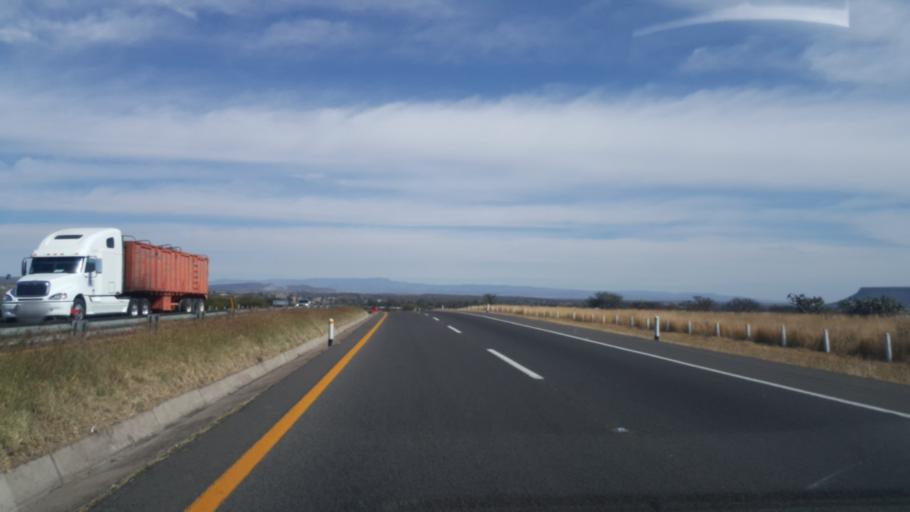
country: MX
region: Jalisco
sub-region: Lagos de Moreno
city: Cristeros [Fraccionamiento]
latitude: 21.3101
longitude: -102.0654
